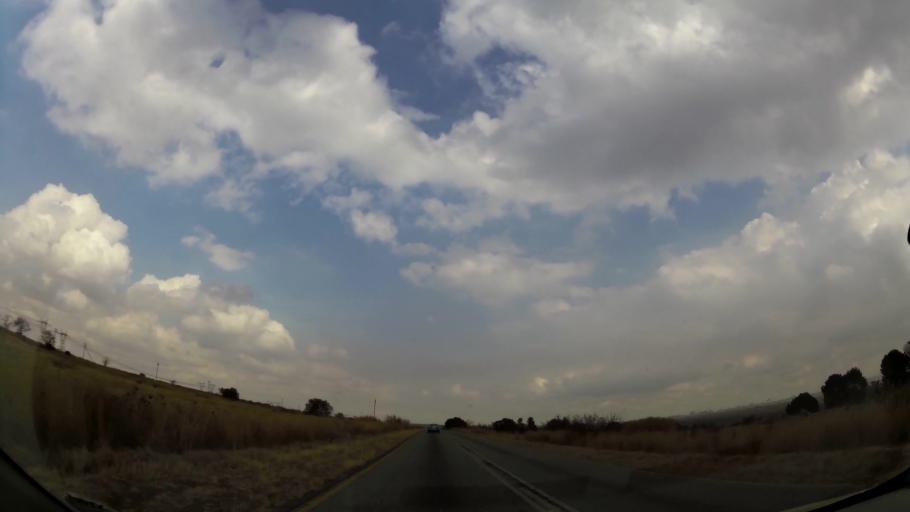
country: ZA
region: Orange Free State
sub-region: Fezile Dabi District Municipality
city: Sasolburg
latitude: -26.7893
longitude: 27.9173
